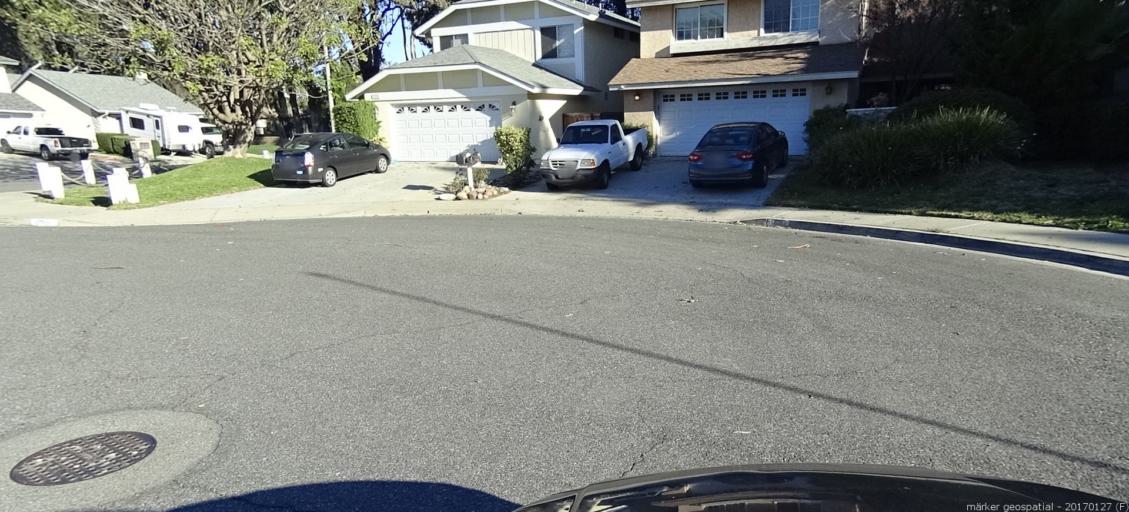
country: US
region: California
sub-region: Orange County
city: Lake Forest
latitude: 33.6518
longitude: -117.6582
